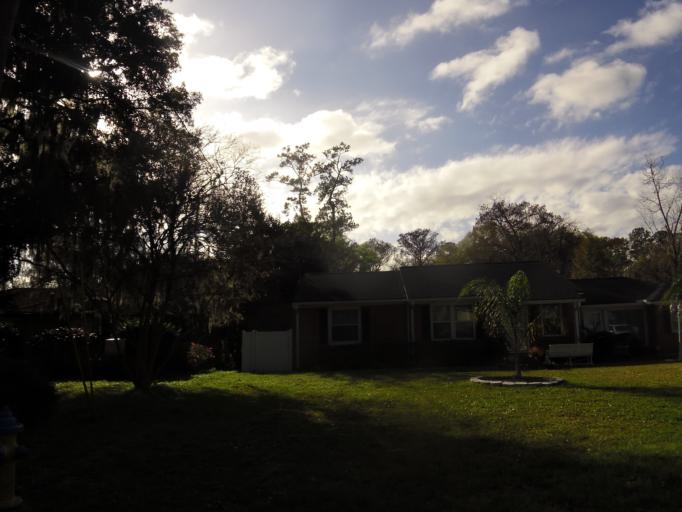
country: US
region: Florida
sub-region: Duval County
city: Jacksonville
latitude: 30.2959
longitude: -81.6183
